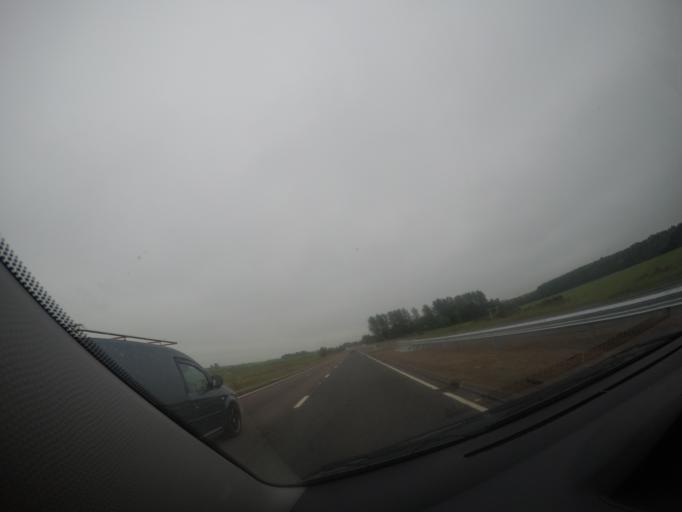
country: GB
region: Scotland
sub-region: Angus
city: Brechin
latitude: 56.7252
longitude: -2.7364
